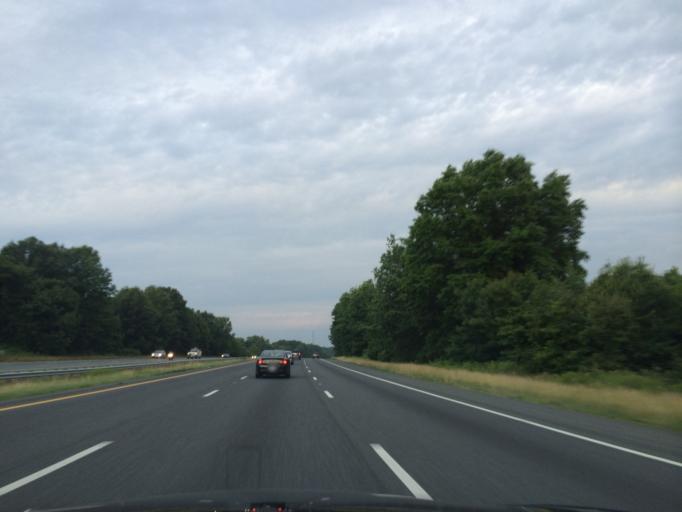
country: US
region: Maryland
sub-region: Carroll County
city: Mount Airy
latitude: 39.3488
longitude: -77.1012
